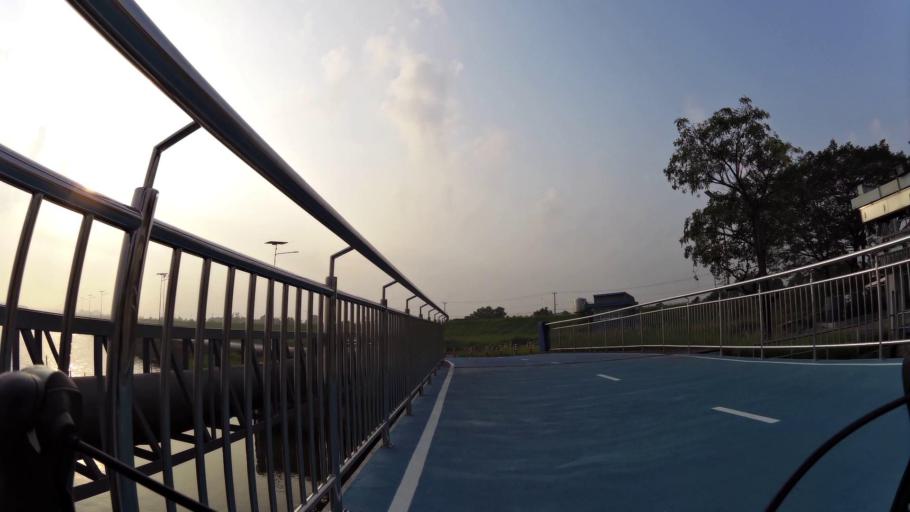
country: TH
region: Bangkok
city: Lat Krabang
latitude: 13.6954
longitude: 100.7739
